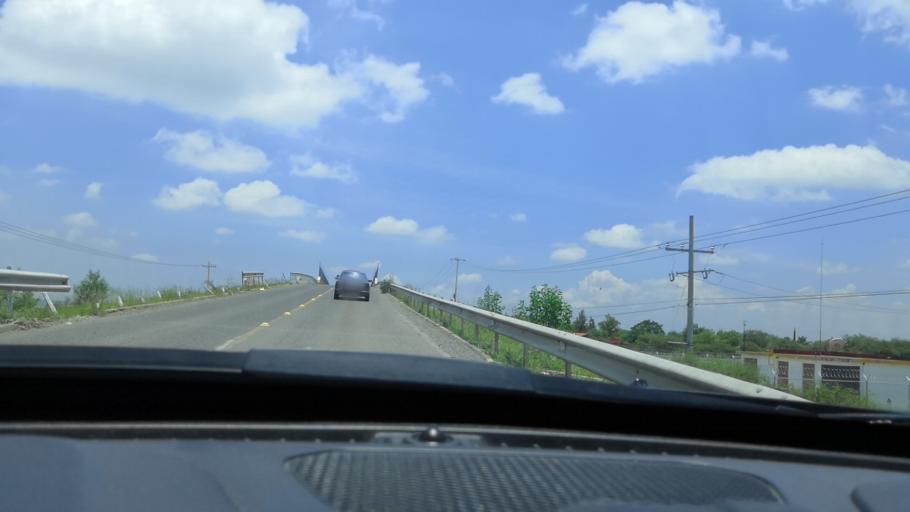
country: MX
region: Guanajuato
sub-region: Silao de la Victoria
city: El Refugio de los Sauces
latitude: 21.0124
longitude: -101.5798
